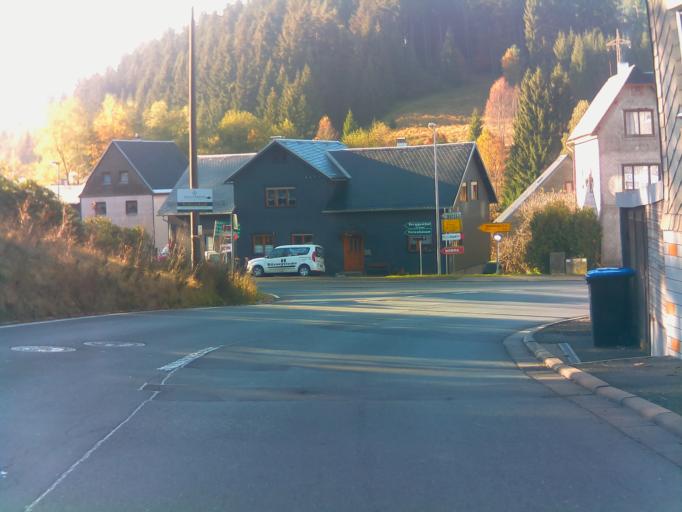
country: DE
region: Thuringia
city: Piesau
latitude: 50.5244
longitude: 11.2232
